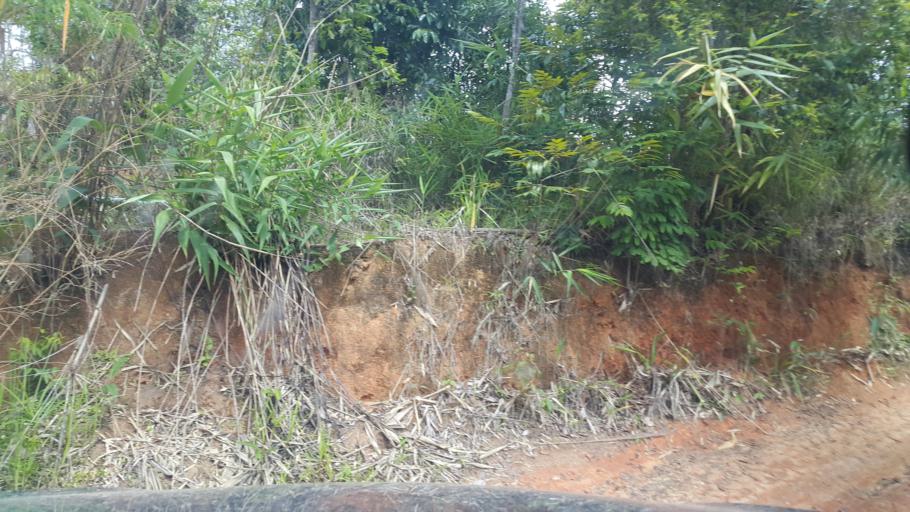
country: TH
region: Loei
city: Na Haeo
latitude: 17.6062
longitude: 100.9053
